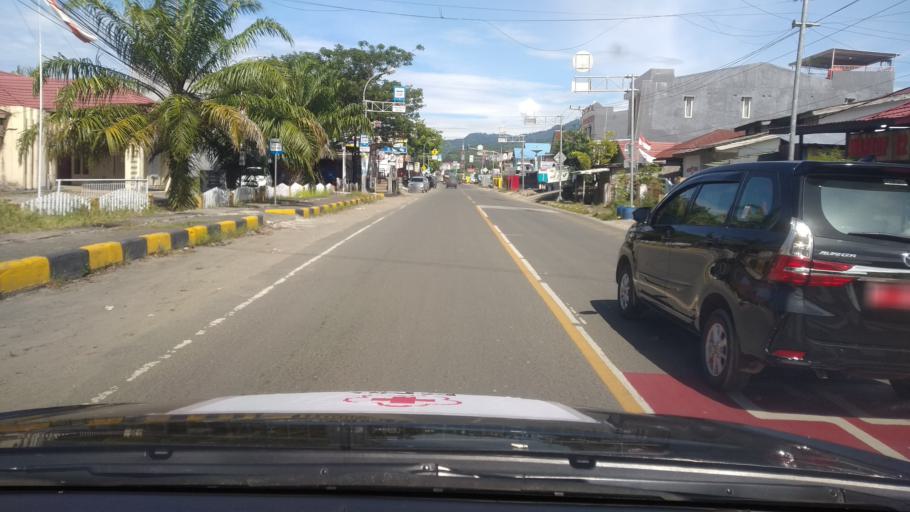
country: ID
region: Sulawesi Barat
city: Mamuju
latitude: -2.6825
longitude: 118.8706
